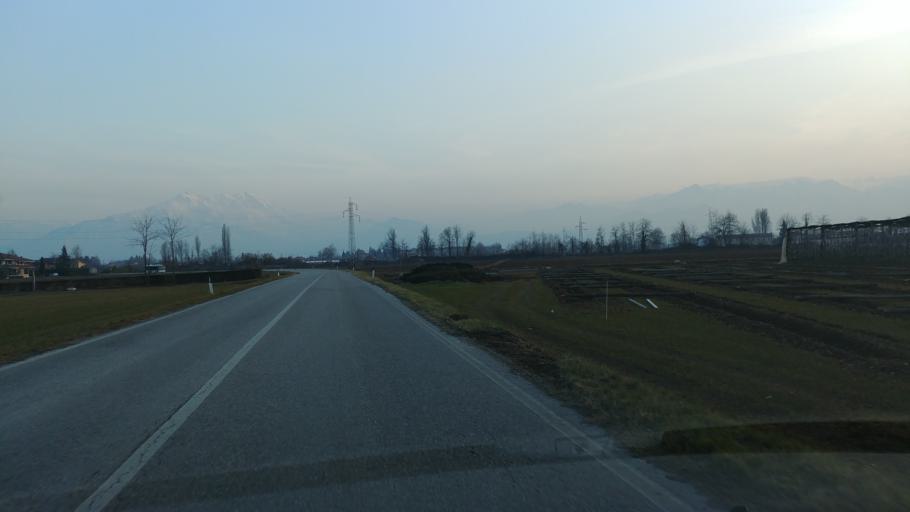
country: IT
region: Piedmont
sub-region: Provincia di Cuneo
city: San Defendente
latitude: 44.4105
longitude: 7.5159
